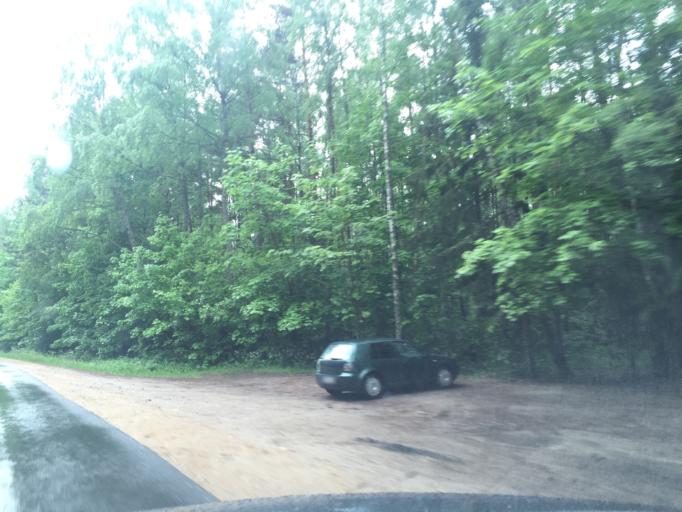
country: LT
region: Klaipedos apskritis
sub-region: Klaipeda
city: Klaipeda
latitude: 55.7916
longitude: 21.0720
